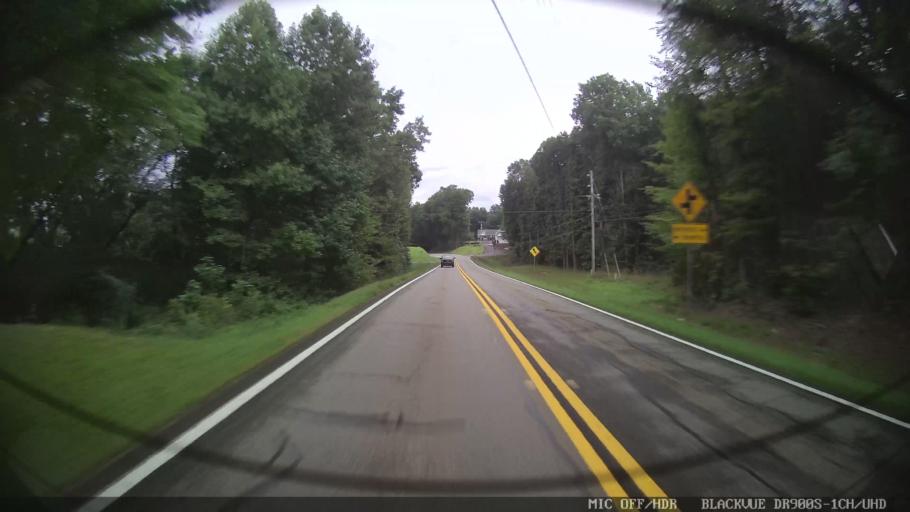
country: US
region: Georgia
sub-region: Gilmer County
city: Ellijay
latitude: 34.7320
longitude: -84.5118
